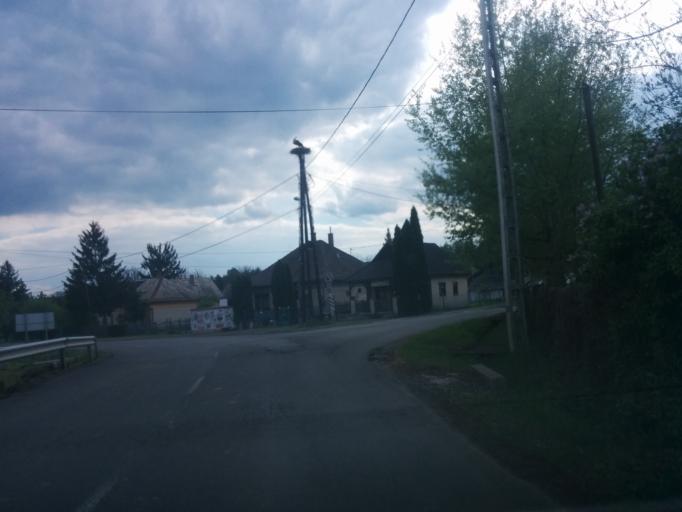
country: HU
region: Nograd
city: Bercel
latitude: 47.8458
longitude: 19.3887
